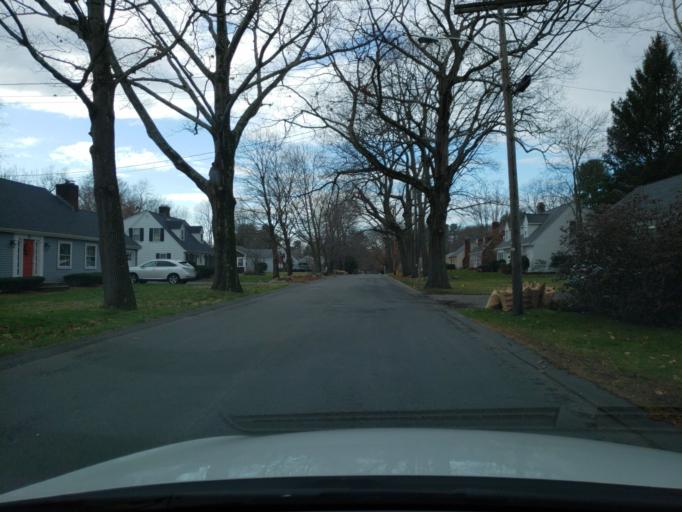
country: US
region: Massachusetts
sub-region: Essex County
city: Andover
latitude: 42.6603
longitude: -71.1206
